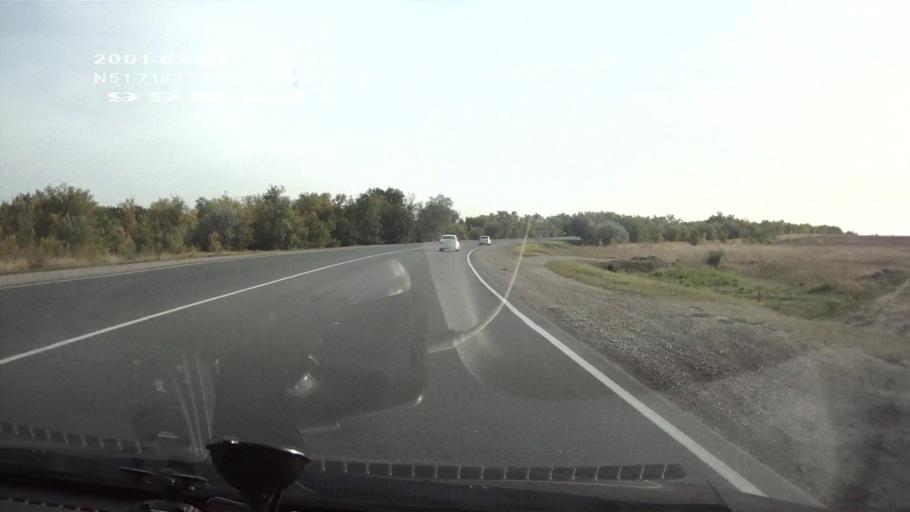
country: RU
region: Saratov
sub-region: Saratovskiy Rayon
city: Saratov
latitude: 51.7187
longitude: 46.0250
